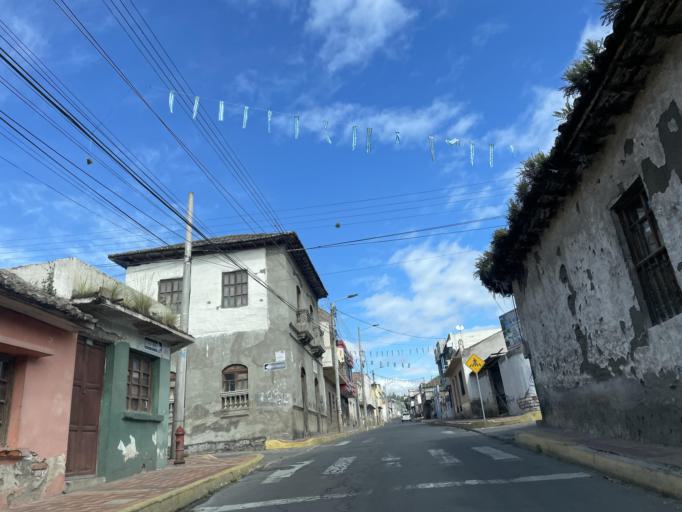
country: EC
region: Chimborazo
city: Guano
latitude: -1.6076
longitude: -78.6395
